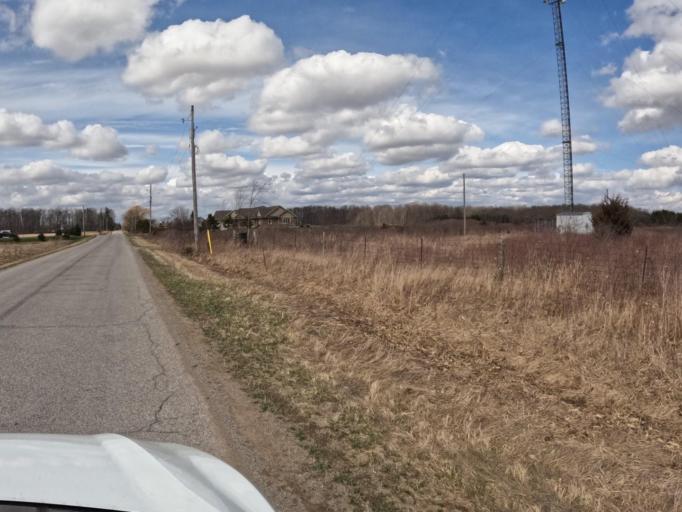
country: CA
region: Ontario
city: Norfolk County
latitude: 42.8689
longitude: -80.1932
